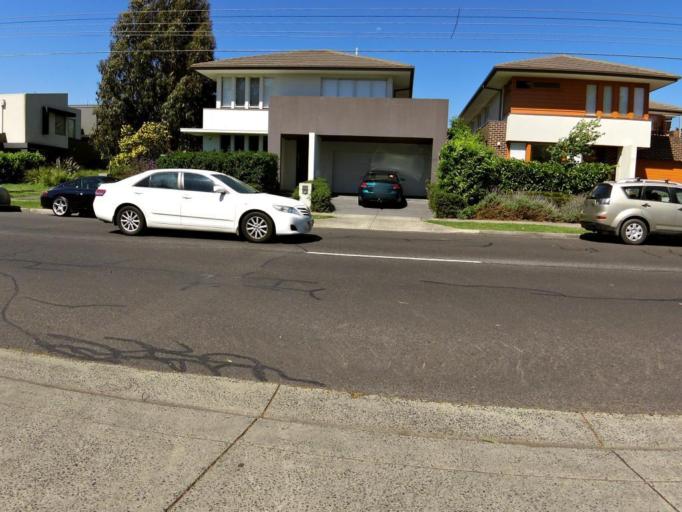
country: AU
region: Victoria
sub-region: Whitehorse
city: Forest Hill
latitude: -37.8485
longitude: 145.1640
